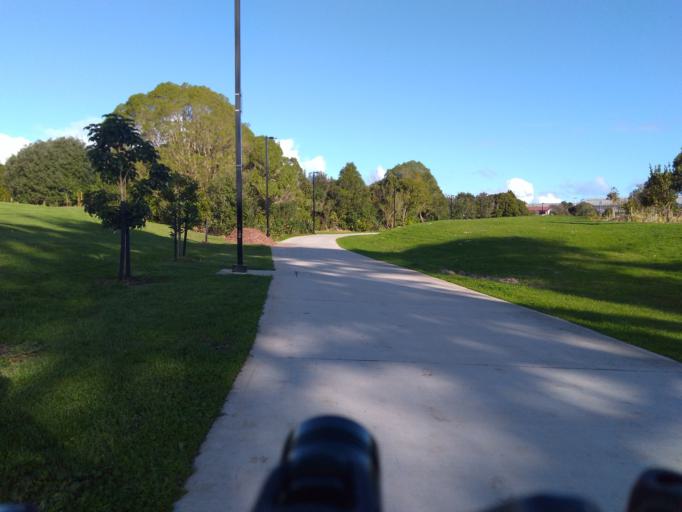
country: NZ
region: Auckland
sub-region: Auckland
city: Rosebank
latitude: -36.8902
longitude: 174.7066
